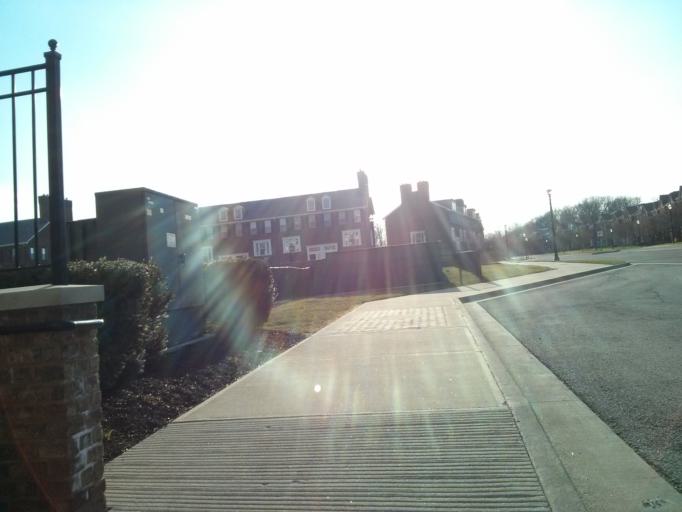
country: US
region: Indiana
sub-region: Hamilton County
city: Carmel
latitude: 39.9703
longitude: -86.1326
